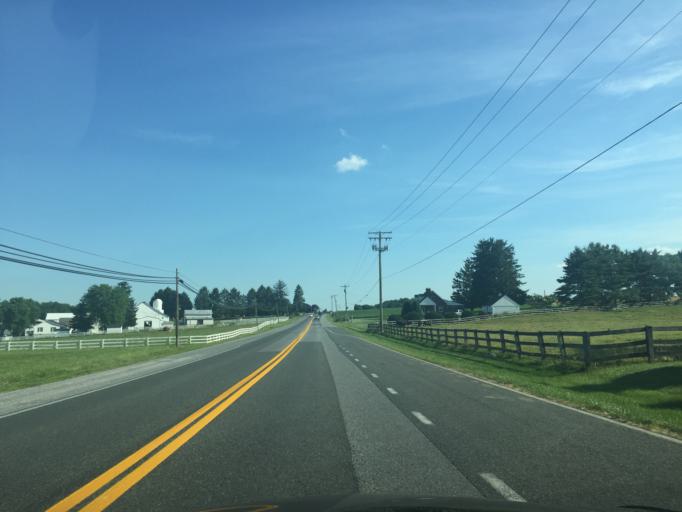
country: US
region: Maryland
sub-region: Harford County
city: Jarrettsville
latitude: 39.6222
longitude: -76.4763
